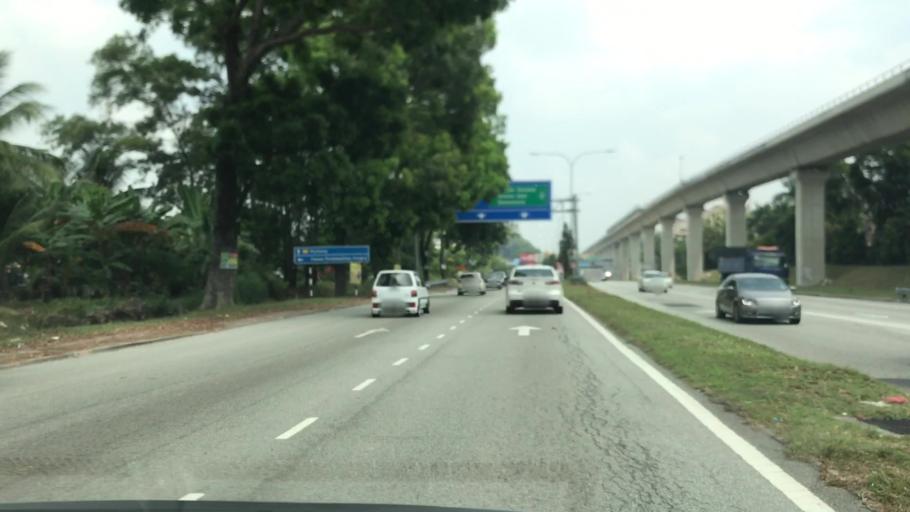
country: MY
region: Selangor
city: Subang Jaya
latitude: 3.0492
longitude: 101.6400
